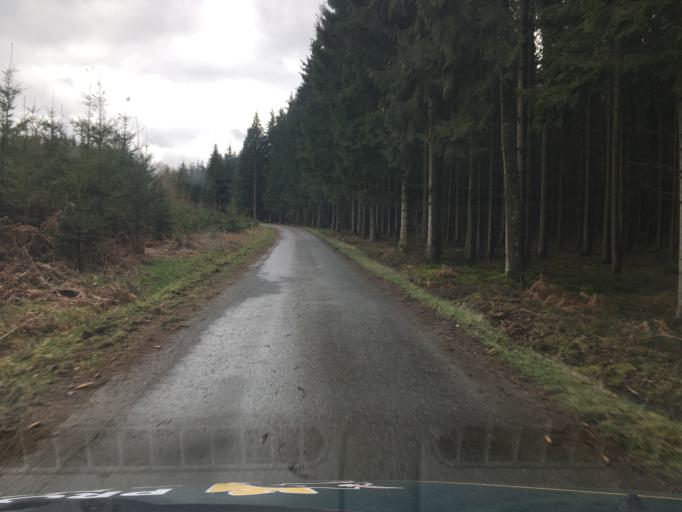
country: FR
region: Champagne-Ardenne
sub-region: Departement des Ardennes
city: Haybes
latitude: 50.0469
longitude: 4.6682
